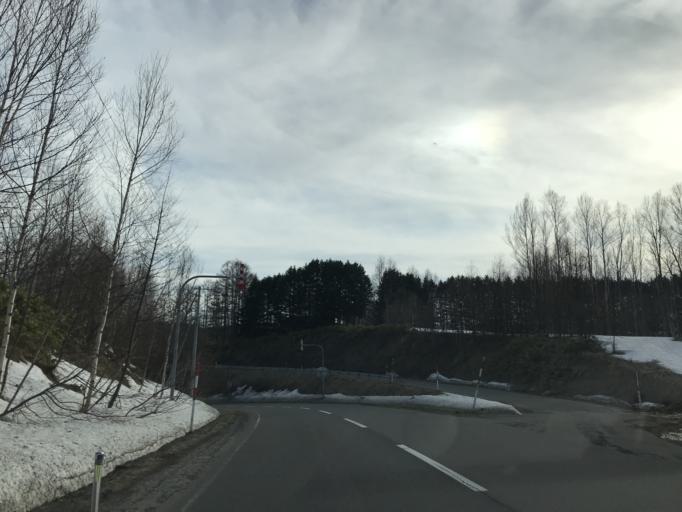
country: JP
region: Hokkaido
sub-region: Asahikawa-shi
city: Asahikawa
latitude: 43.7002
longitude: 142.3244
